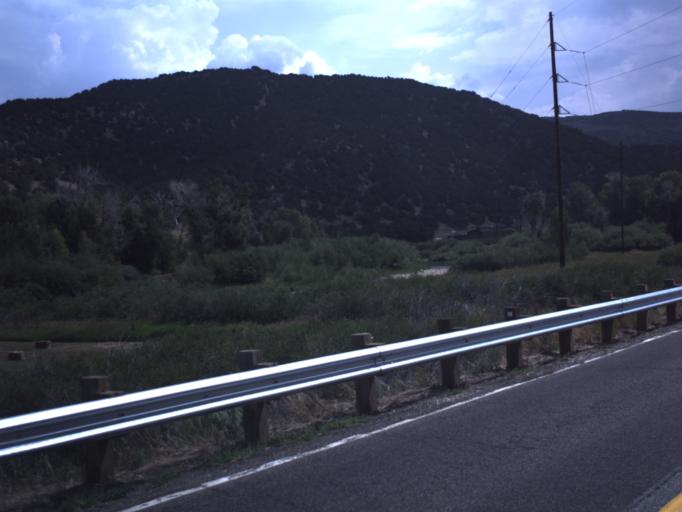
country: US
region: Utah
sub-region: Summit County
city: Oakley
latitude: 40.7523
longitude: -111.3745
